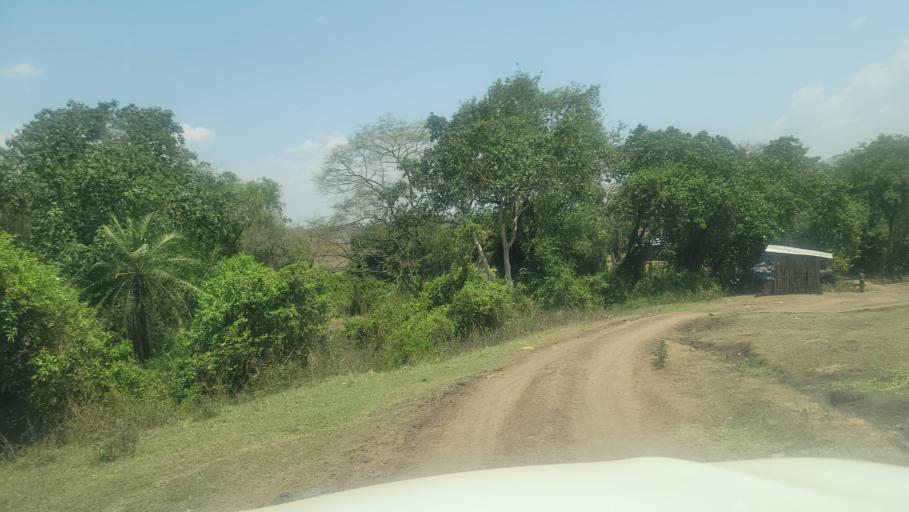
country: ET
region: Southern Nations, Nationalities, and People's Region
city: Bonga
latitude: 7.4969
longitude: 36.2975
